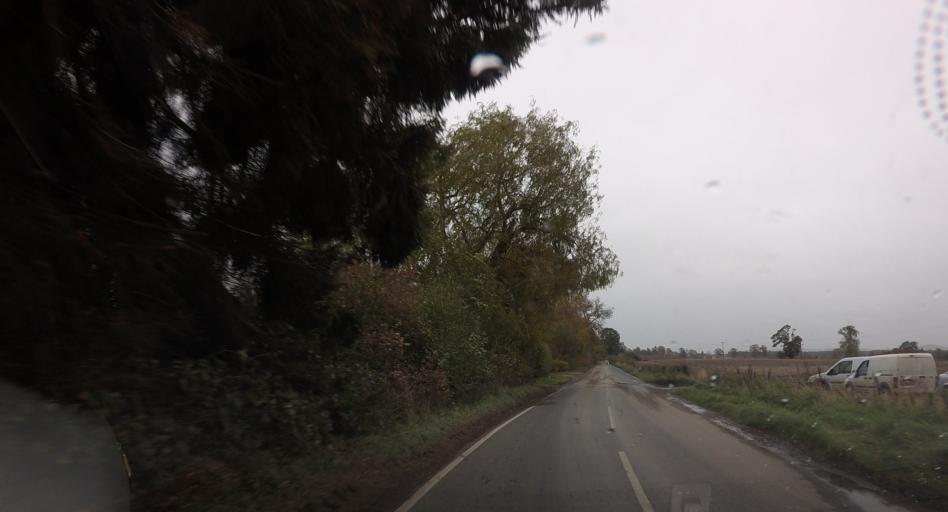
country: GB
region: Scotland
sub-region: Perth and Kinross
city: Stanley
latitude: 56.5549
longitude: -3.4142
